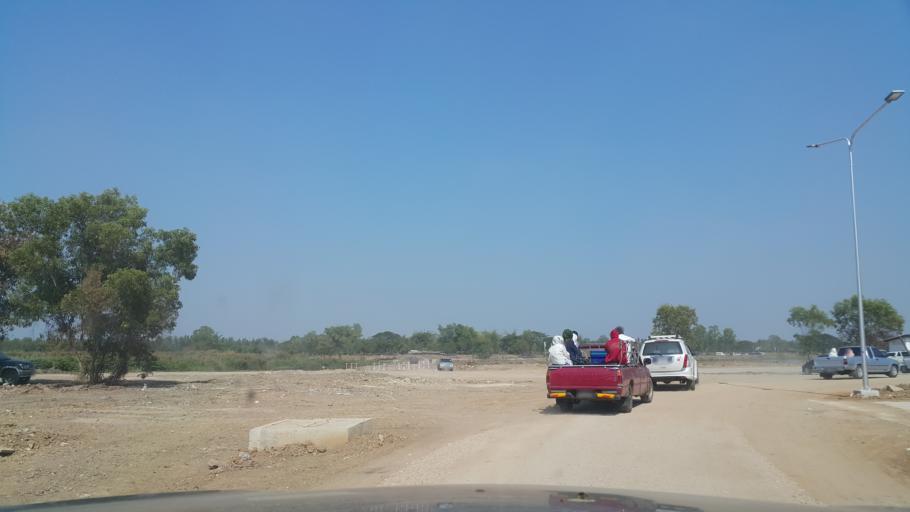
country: TH
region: Khon Kaen
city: Khon Kaen
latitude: 16.5132
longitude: 102.8677
